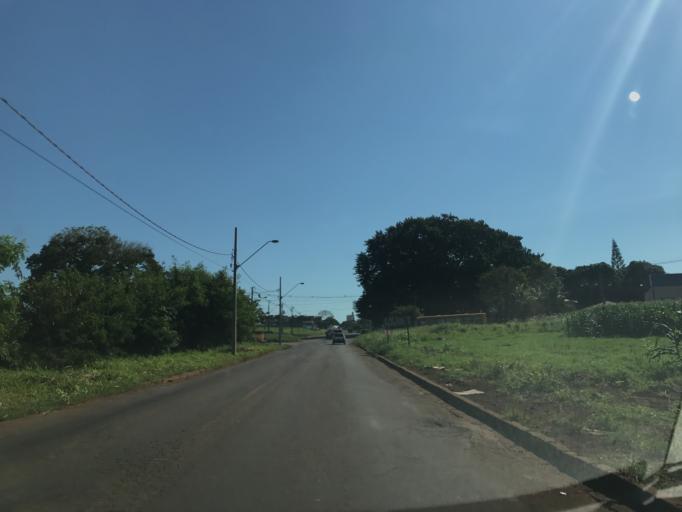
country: BR
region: Parana
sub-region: Maringa
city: Maringa
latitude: -23.4574
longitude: -51.9527
